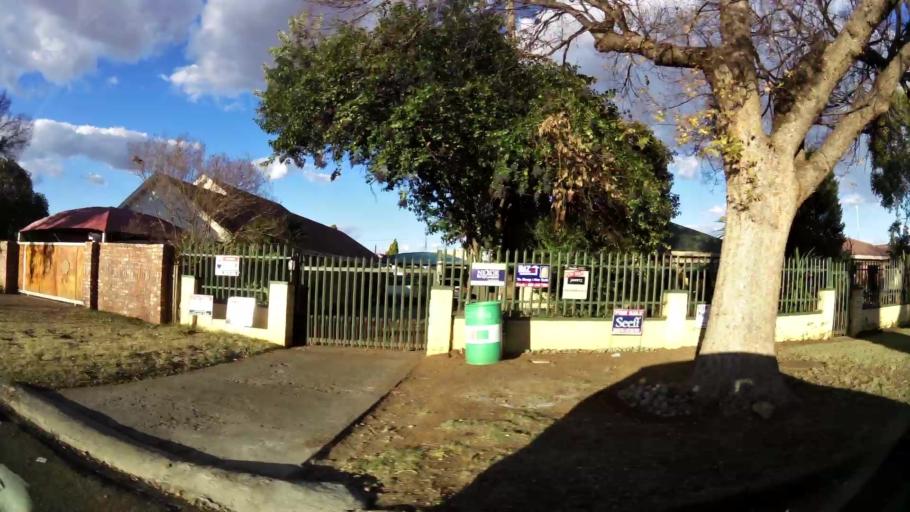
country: ZA
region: North-West
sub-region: Dr Kenneth Kaunda District Municipality
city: Potchefstroom
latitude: -26.7230
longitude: 27.1004
